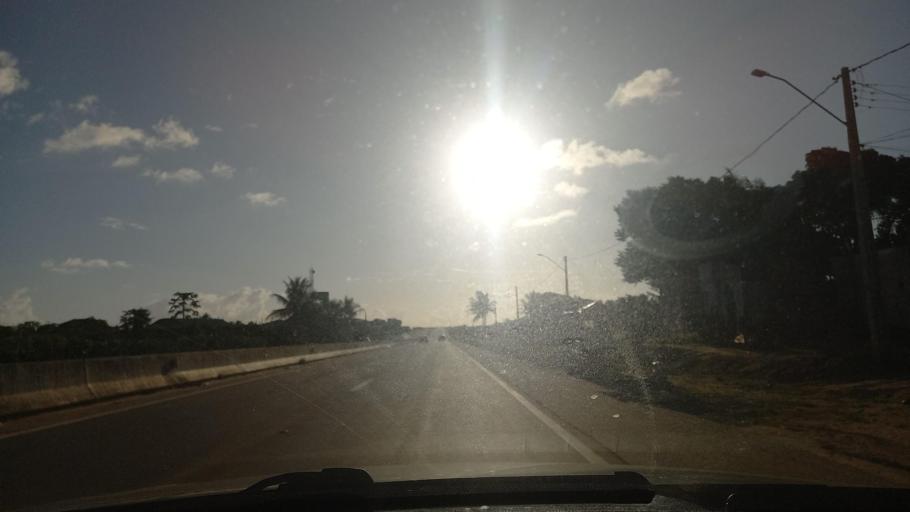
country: BR
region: Alagoas
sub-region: Campo Alegre
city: Campo Alegre
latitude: -9.8028
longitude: -36.2733
